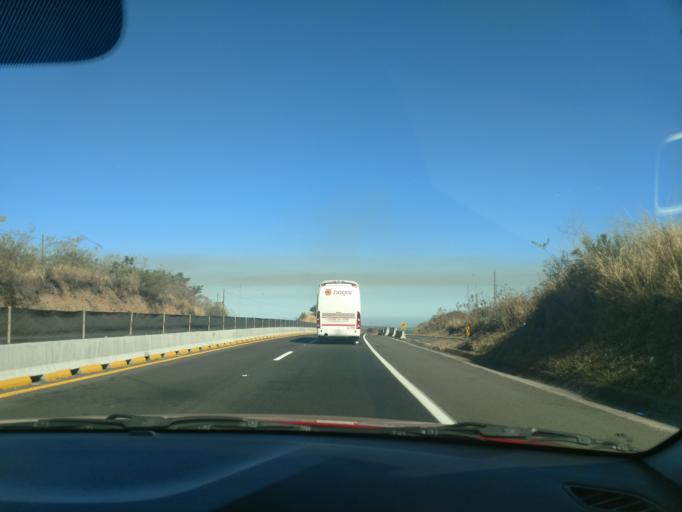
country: MX
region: Nayarit
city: Tepic
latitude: 21.5601
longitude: -104.9684
